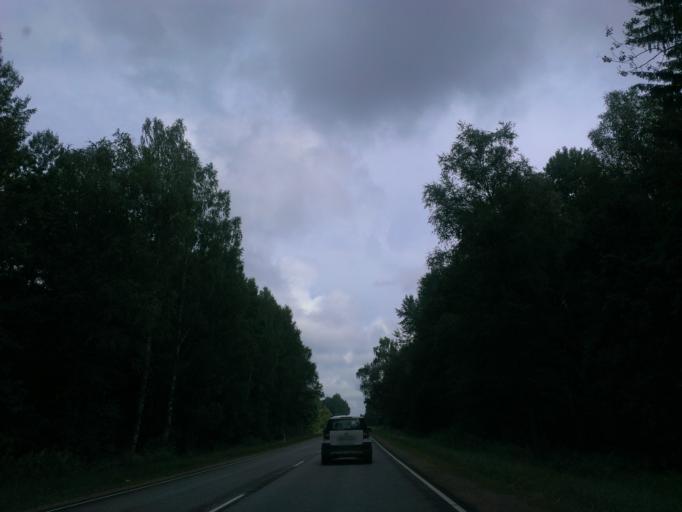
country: LV
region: Ligatne
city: Ligatne
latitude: 57.1822
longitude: 25.0071
